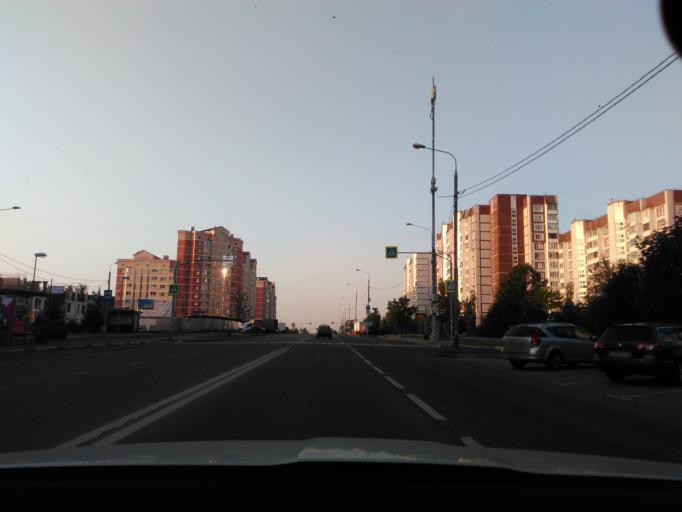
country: RU
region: Moscow
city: Zelenograd
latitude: 55.9745
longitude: 37.1620
